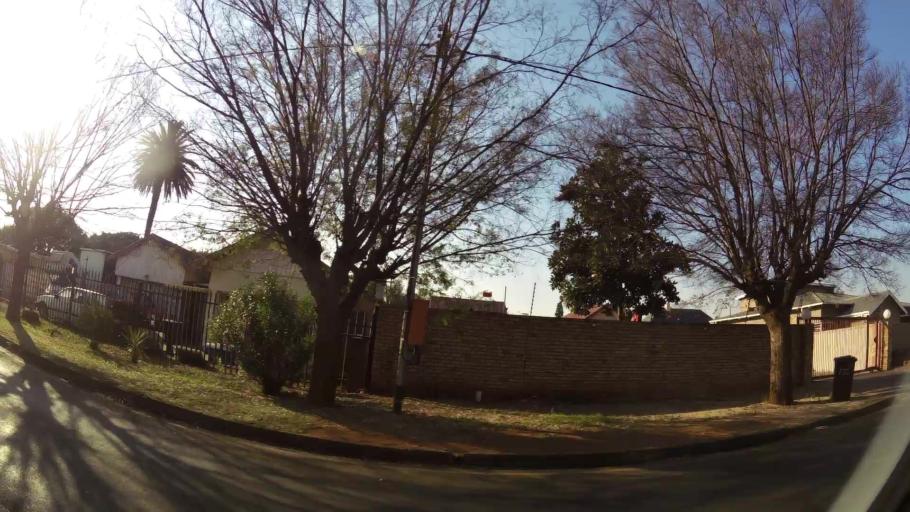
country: ZA
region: Gauteng
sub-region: Ekurhuleni Metropolitan Municipality
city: Brakpan
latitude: -26.2503
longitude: 28.3713
